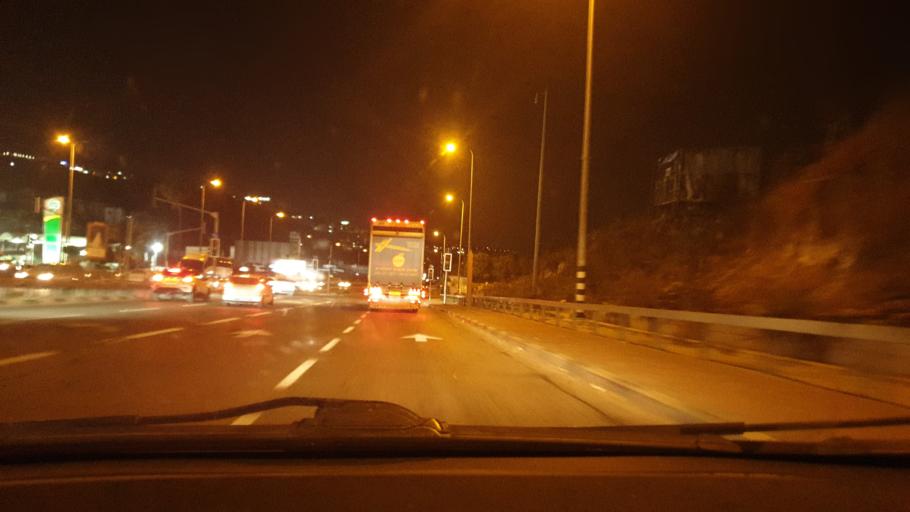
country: IL
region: Haifa
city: Umm el Fahm
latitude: 32.5338
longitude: 35.1480
